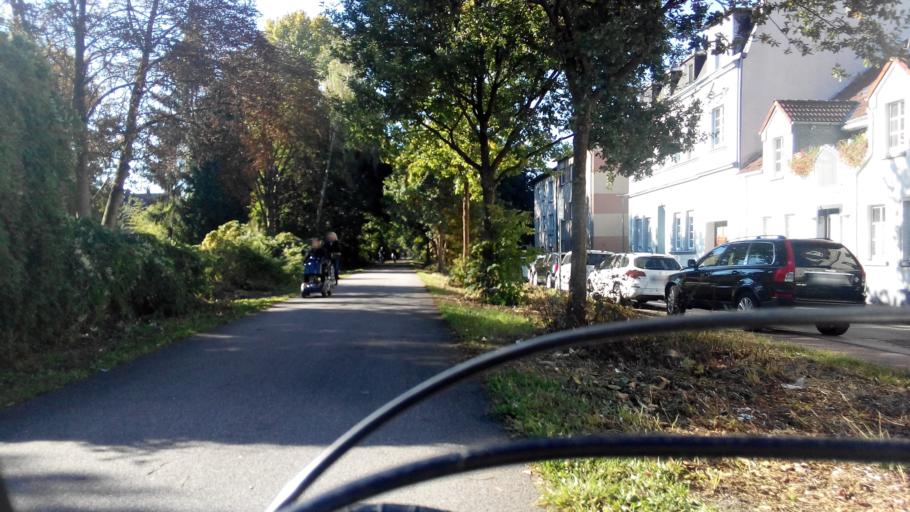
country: DE
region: North Rhine-Westphalia
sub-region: Regierungsbezirk Munster
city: Gelsenkirchen
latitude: 51.4971
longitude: 7.1214
